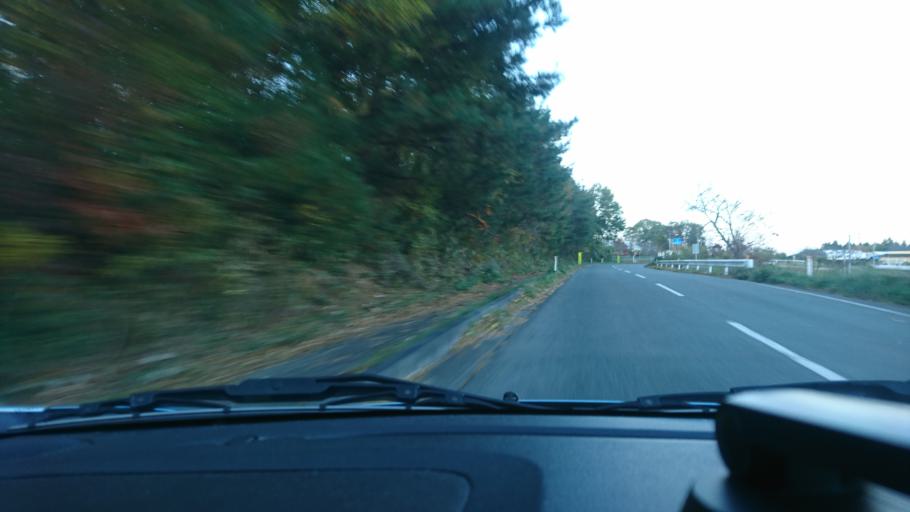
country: JP
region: Iwate
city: Ichinoseki
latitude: 38.7719
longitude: 141.2411
